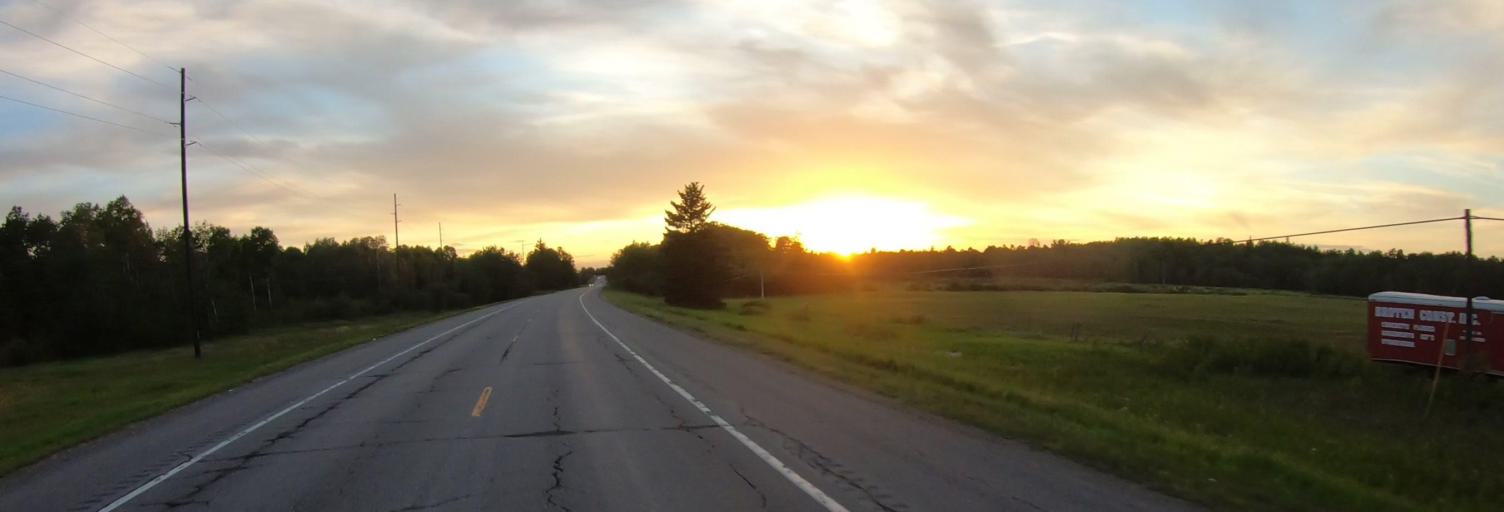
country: US
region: Minnesota
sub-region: Saint Louis County
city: Aurora
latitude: 47.7968
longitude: -92.3121
